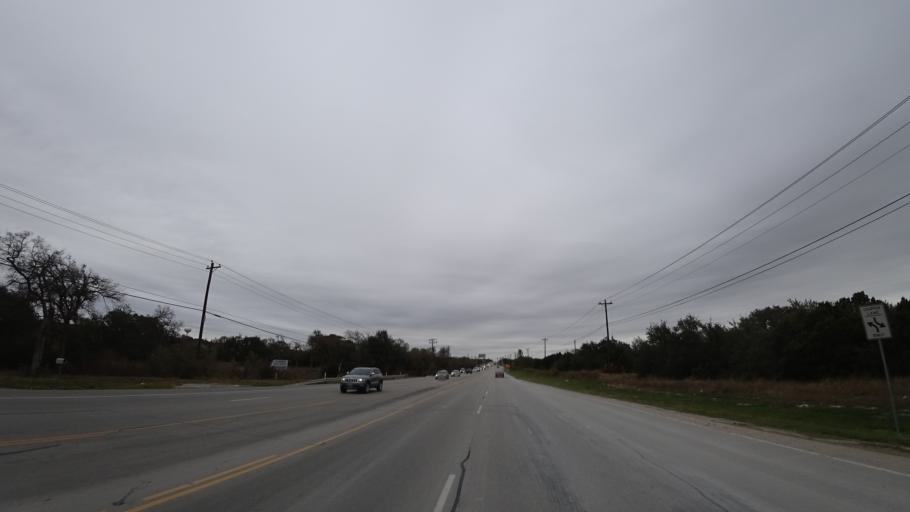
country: US
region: Texas
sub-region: Williamson County
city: Cedar Park
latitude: 30.5129
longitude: -97.8561
